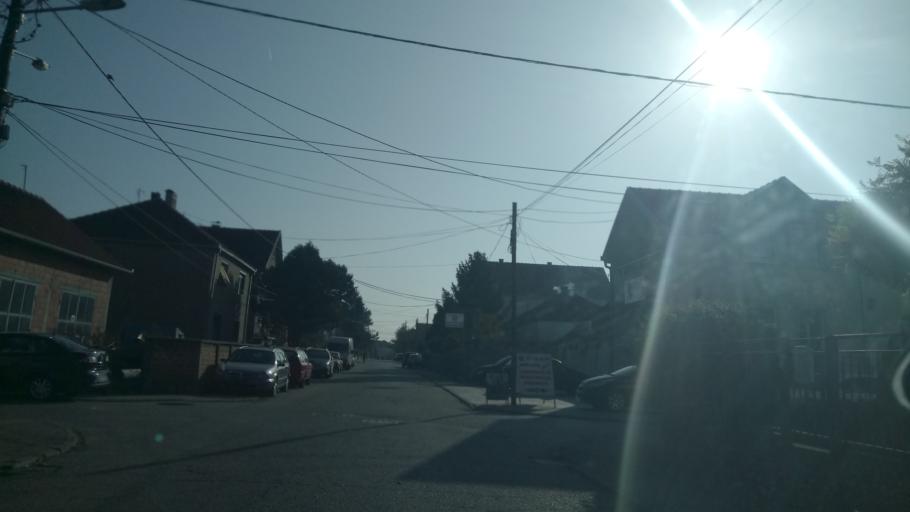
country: RS
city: Novi Banovci
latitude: 44.9048
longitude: 20.2863
